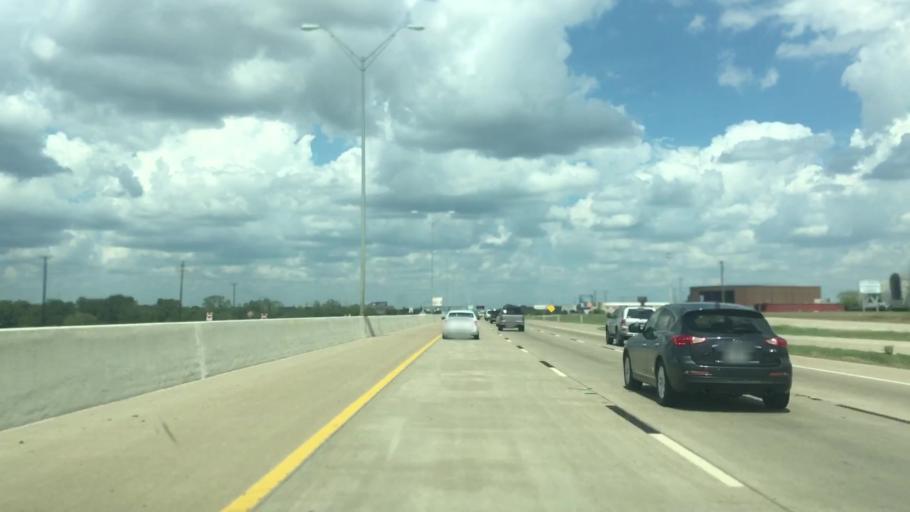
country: US
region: Texas
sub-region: McLennan County
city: Hewitt
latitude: 31.4623
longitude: -97.1698
